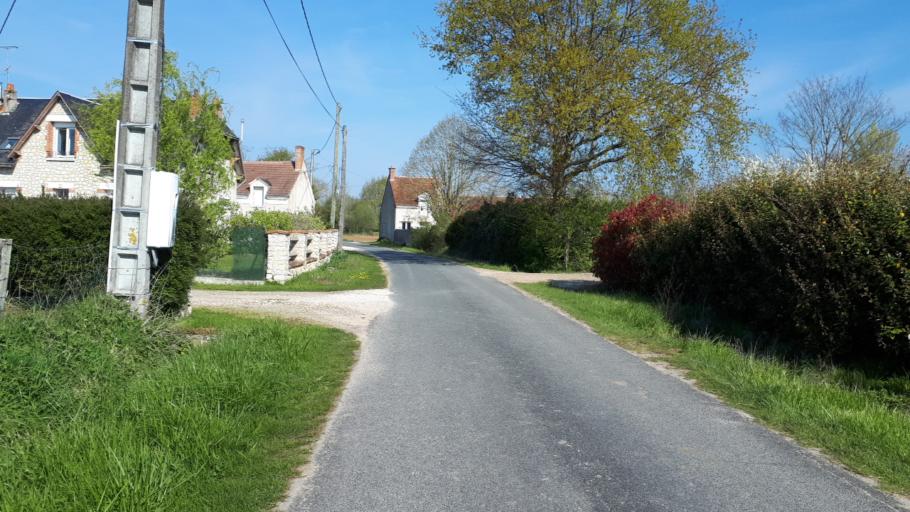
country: FR
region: Centre
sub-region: Departement du Loir-et-Cher
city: Contres
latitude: 47.3813
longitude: 1.3923
